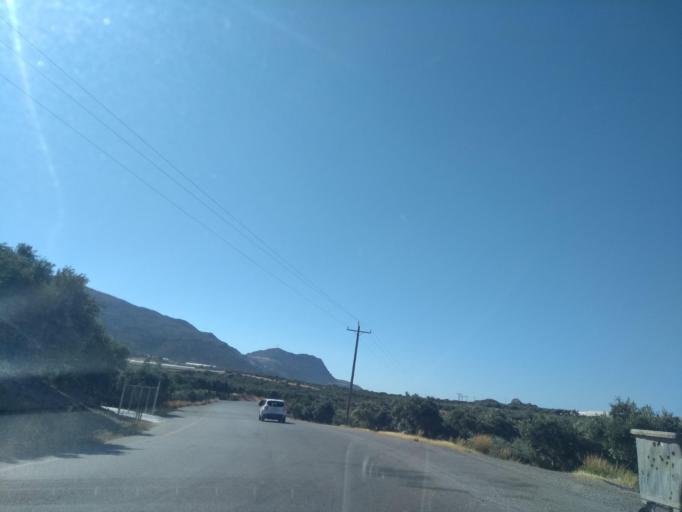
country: GR
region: Crete
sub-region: Nomos Chanias
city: Palaiochora
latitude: 35.2975
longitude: 23.5399
